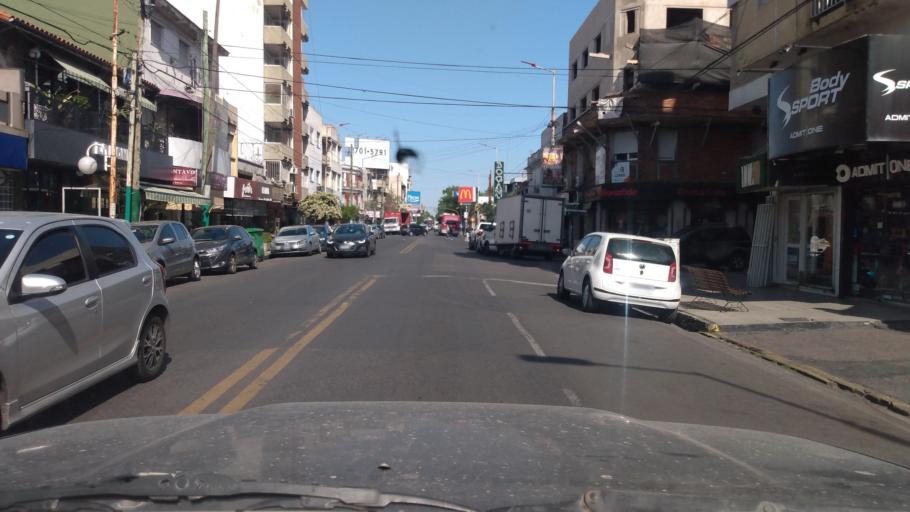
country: AR
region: Buenos Aires
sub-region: Partido de Moron
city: Moron
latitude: -34.6460
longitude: -58.5929
